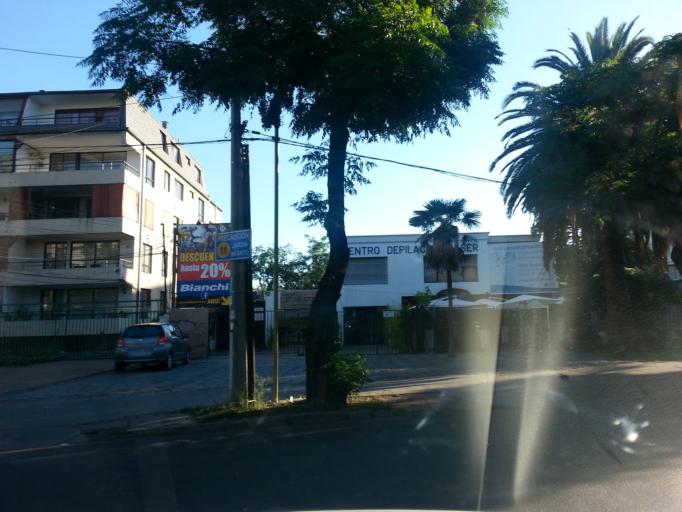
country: CL
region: Santiago Metropolitan
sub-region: Provincia de Santiago
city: Villa Presidente Frei, Nunoa, Santiago, Chile
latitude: -33.4252
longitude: -70.5778
